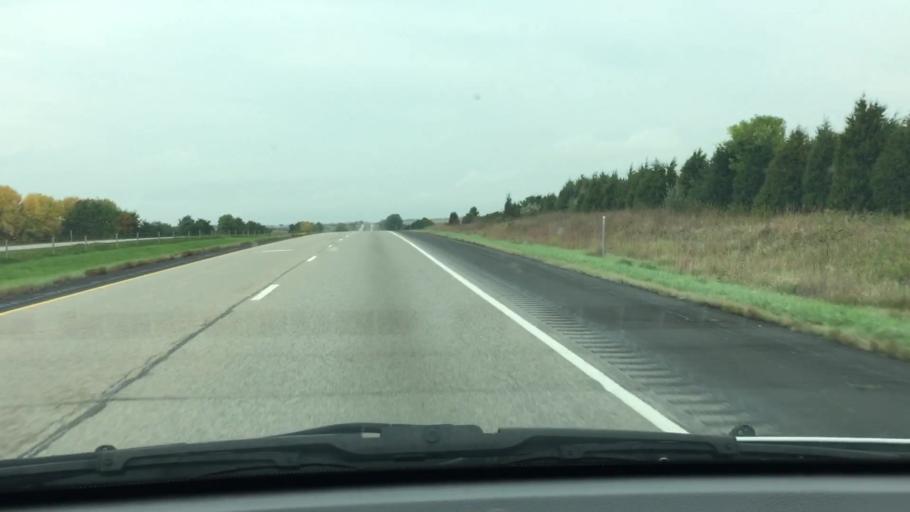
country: US
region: Iowa
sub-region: Muscatine County
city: West Liberty
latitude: 41.6592
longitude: -91.2063
